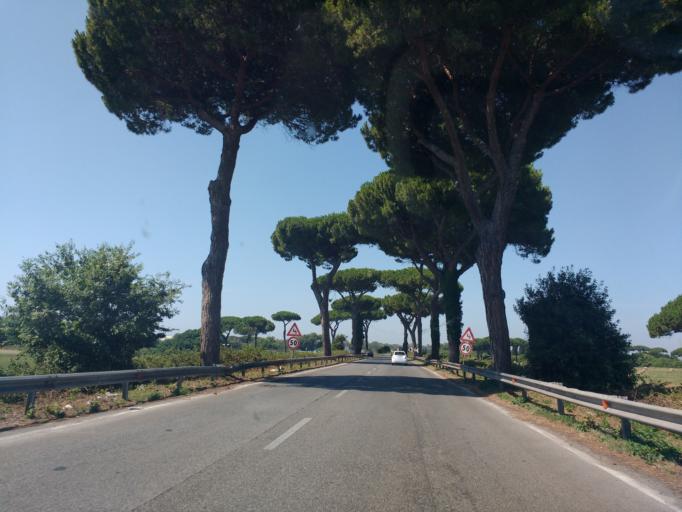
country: IT
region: Latium
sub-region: Citta metropolitana di Roma Capitale
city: Lido di Ostia
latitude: 41.7520
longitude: 12.2912
